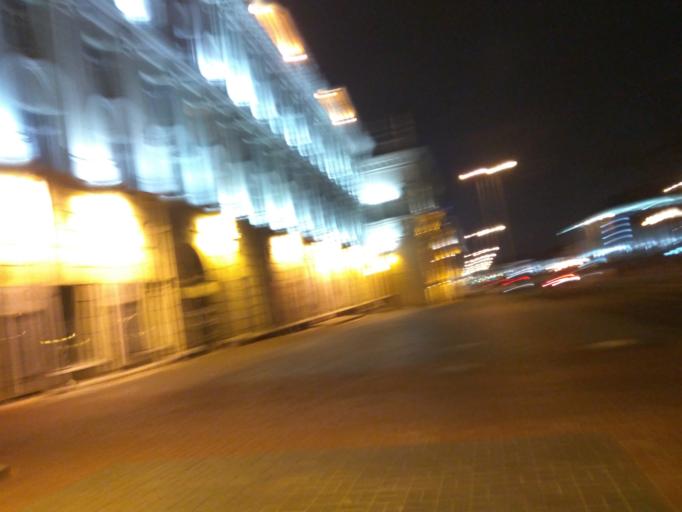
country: BY
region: Minsk
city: Minsk
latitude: 53.9005
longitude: 27.5621
